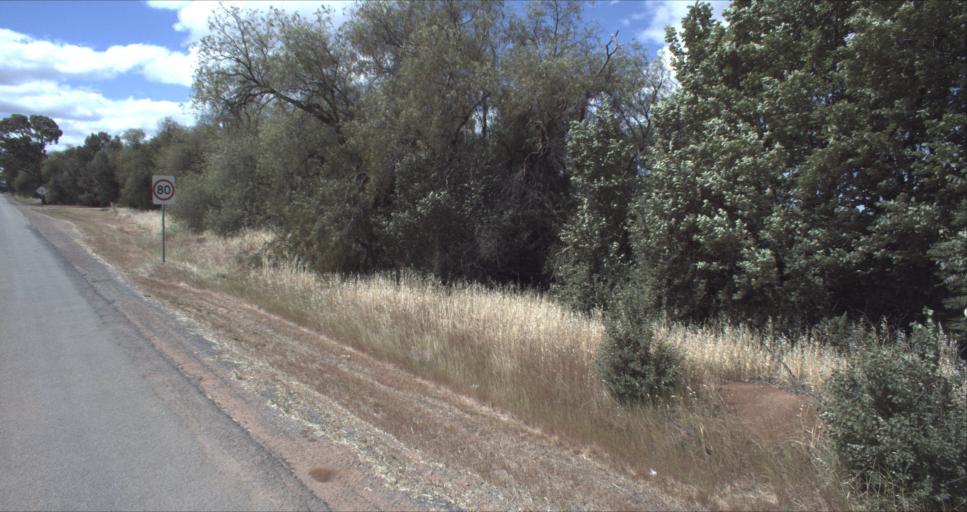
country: AU
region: New South Wales
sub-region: Leeton
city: Leeton
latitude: -34.5895
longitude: 146.3954
